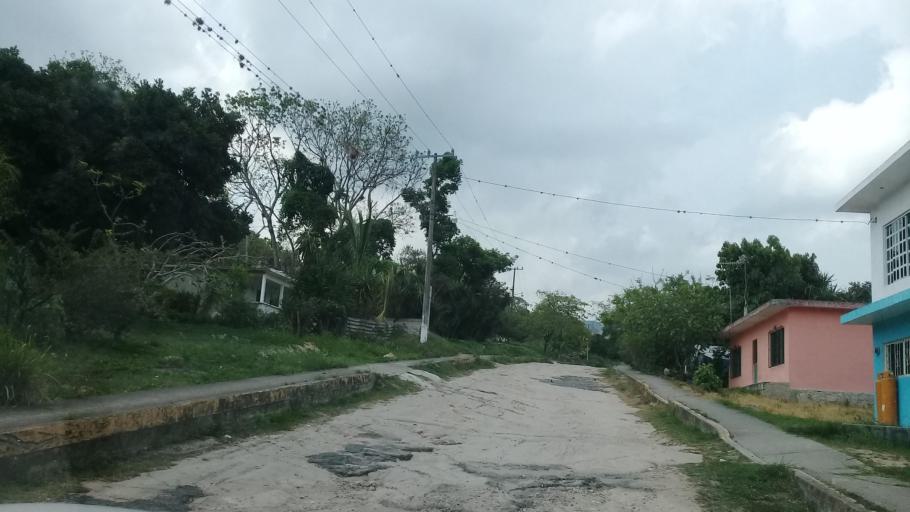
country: MX
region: Veracruz
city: Jalcomulco
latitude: 19.3874
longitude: -96.7939
